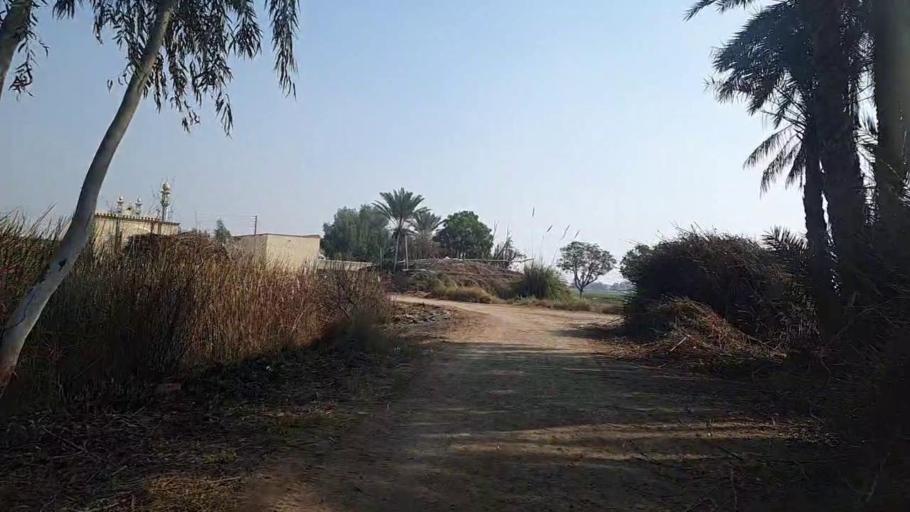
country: PK
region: Sindh
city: Khairpur
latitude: 27.9256
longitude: 69.6685
